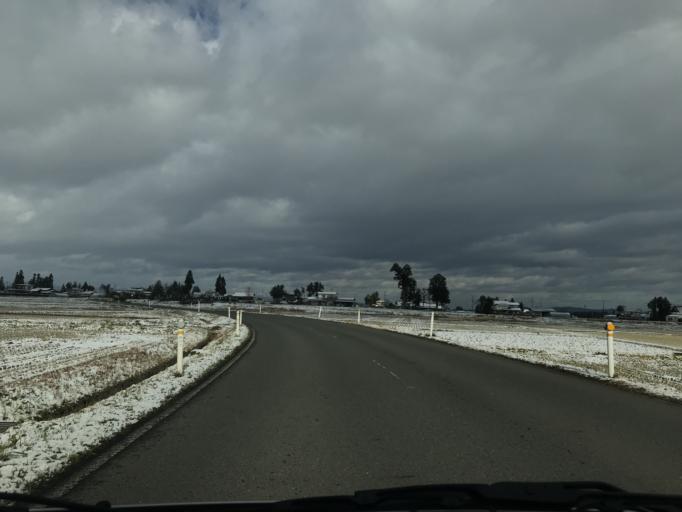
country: JP
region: Iwate
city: Mizusawa
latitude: 39.1558
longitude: 141.1135
